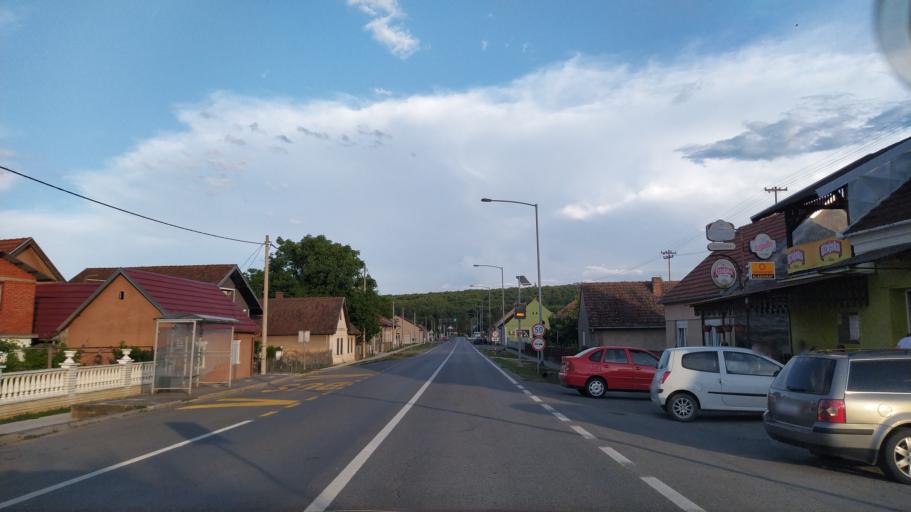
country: HR
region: Osjecko-Baranjska
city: Martin
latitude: 45.4951
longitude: 18.0194
